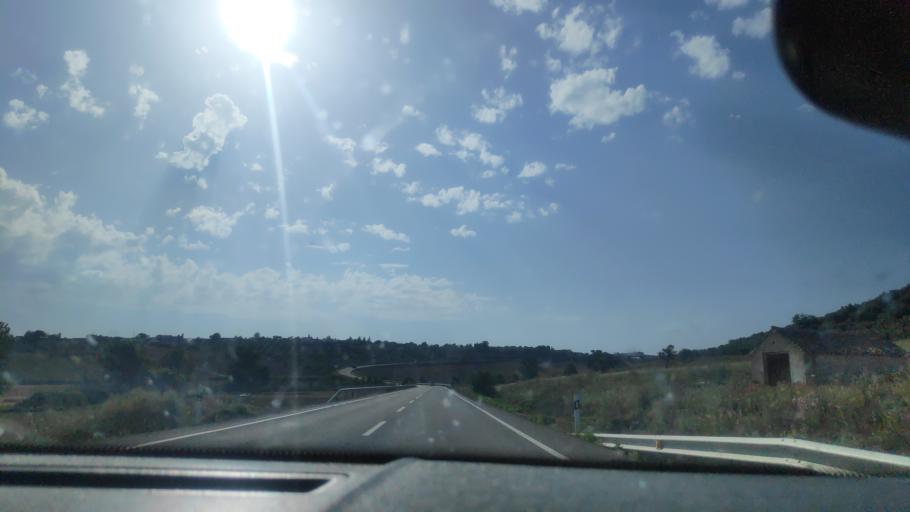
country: ES
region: Andalusia
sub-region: Provincia de Jaen
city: Frailes
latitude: 37.4447
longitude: -3.8598
